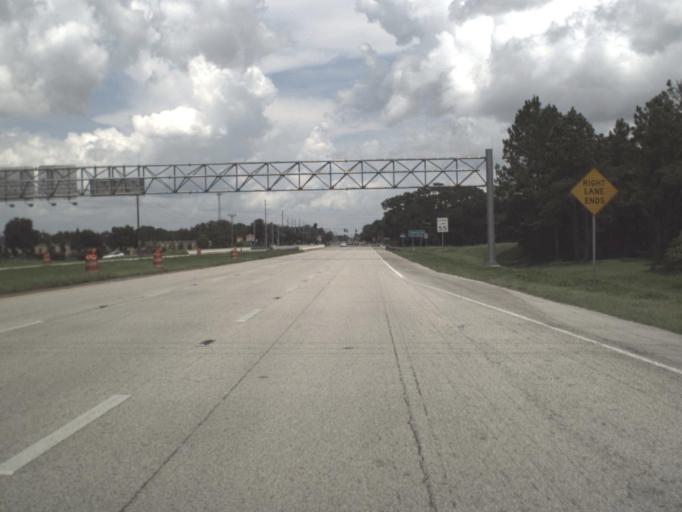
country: US
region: Florida
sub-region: Hillsborough County
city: Temple Terrace
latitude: 28.0541
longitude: -82.3478
